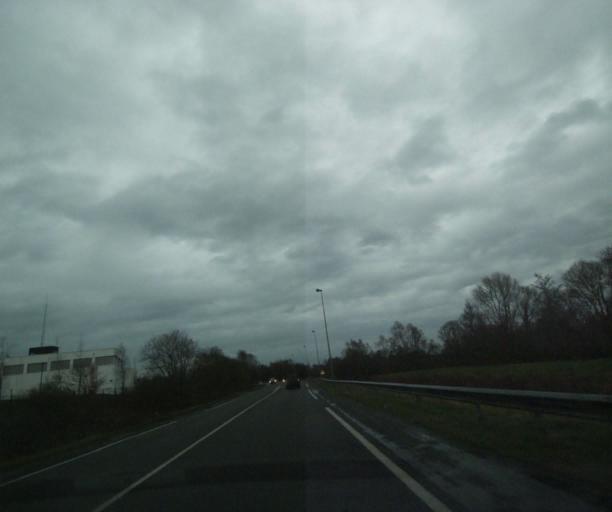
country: FR
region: Nord-Pas-de-Calais
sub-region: Departement du Nord
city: Vieux-Conde
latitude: 50.4503
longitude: 3.5738
